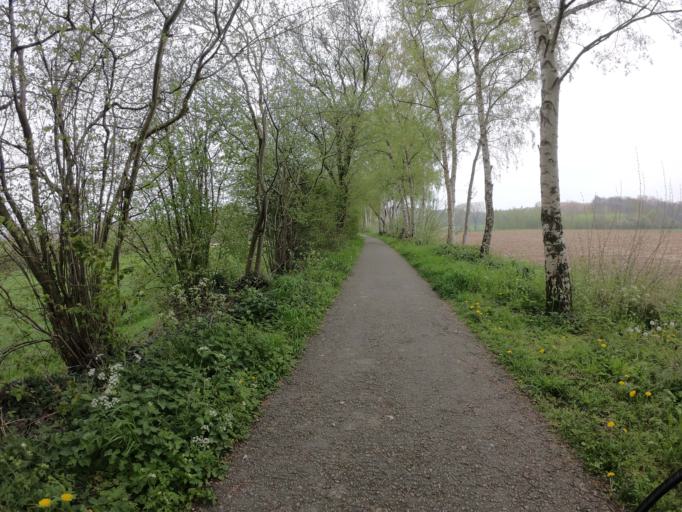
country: BE
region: Flanders
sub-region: Provincie Oost-Vlaanderen
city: Ronse
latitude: 50.7372
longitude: 3.6324
